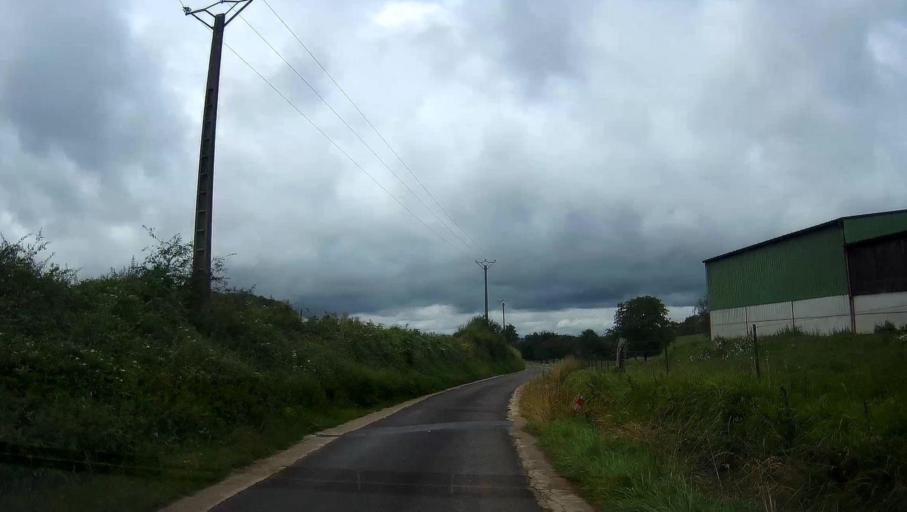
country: FR
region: Champagne-Ardenne
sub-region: Departement des Ardennes
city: Rimogne
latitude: 49.7674
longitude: 4.4888
